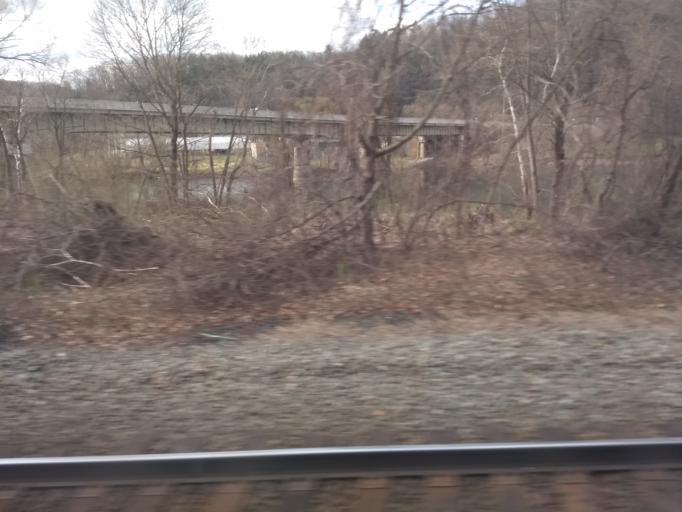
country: US
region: Pennsylvania
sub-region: Huntingdon County
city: Huntingdon
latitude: 40.4774
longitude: -78.0006
